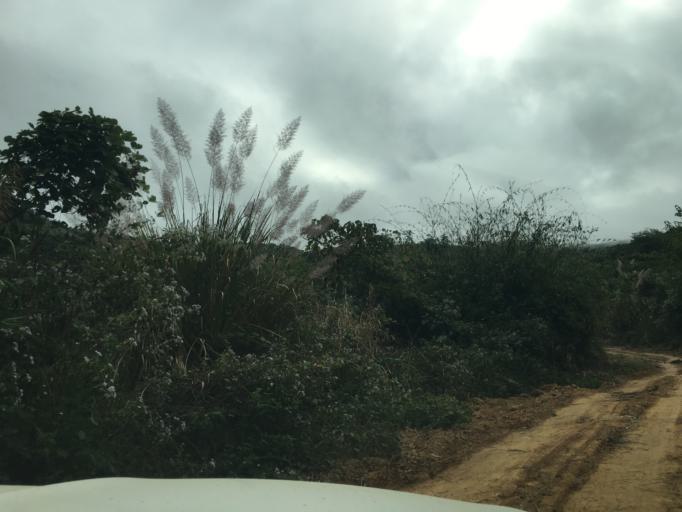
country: LA
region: Houaphan
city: Viengthong
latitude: 19.9394
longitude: 103.2927
